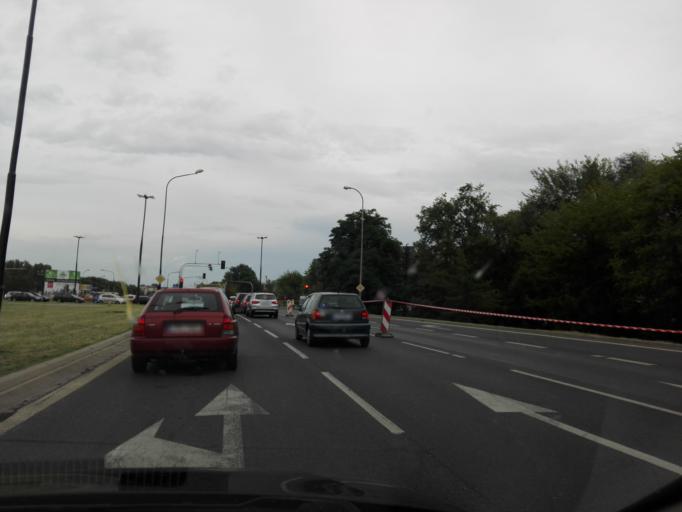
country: PL
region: Lublin Voivodeship
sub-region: Powiat lubelski
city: Lublin
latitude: 51.2531
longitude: 22.5503
